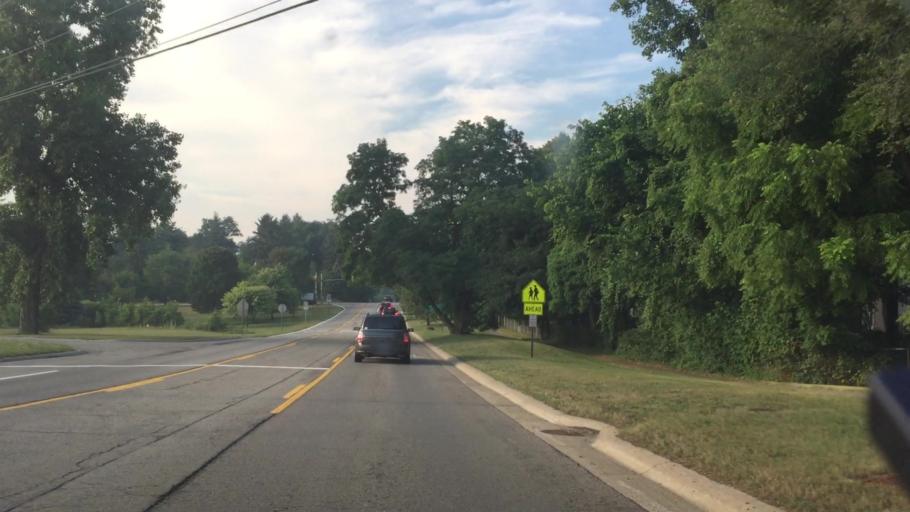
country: US
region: Michigan
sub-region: Oakland County
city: Bloomfield Hills
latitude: 42.5983
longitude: -83.2477
